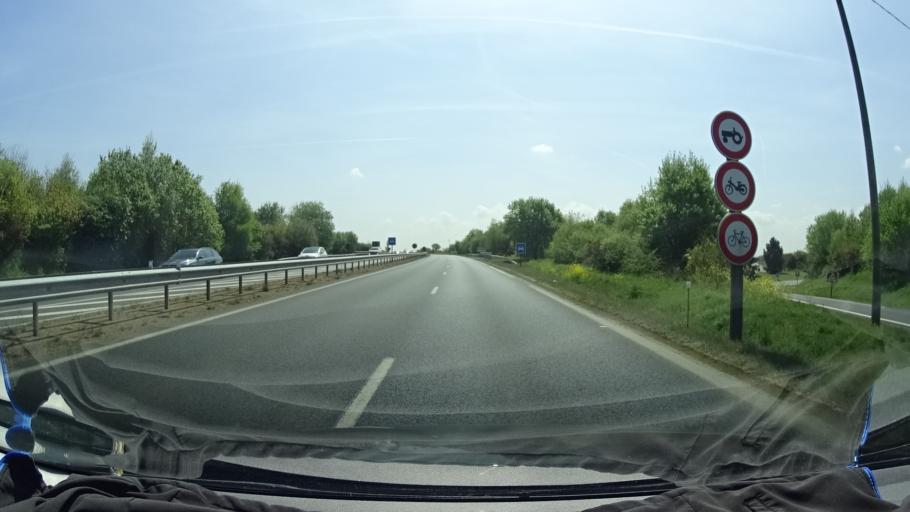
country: FR
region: Brittany
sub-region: Departement des Cotes-d'Armor
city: Plehedel
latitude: 48.7145
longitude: -3.0238
